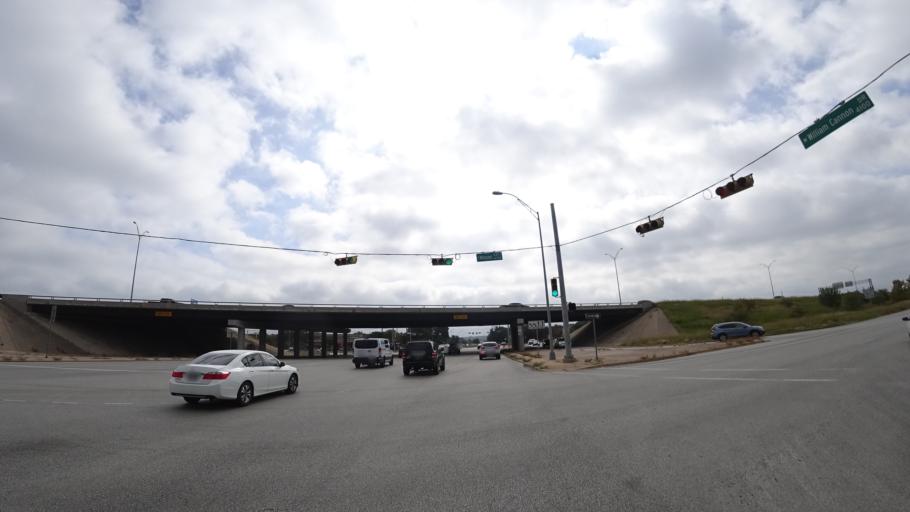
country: US
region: Texas
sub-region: Travis County
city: Shady Hollow
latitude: 30.2208
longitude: -97.8372
